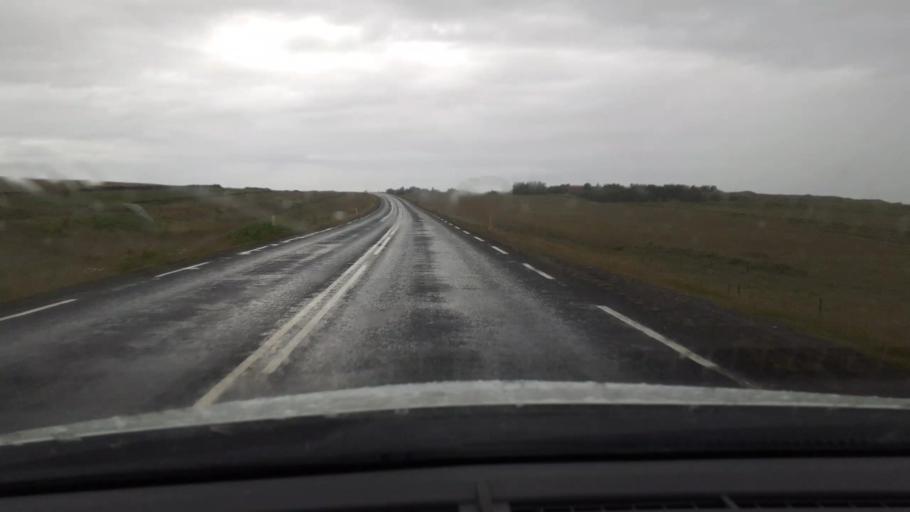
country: IS
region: West
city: Akranes
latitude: 64.3657
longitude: -21.9309
